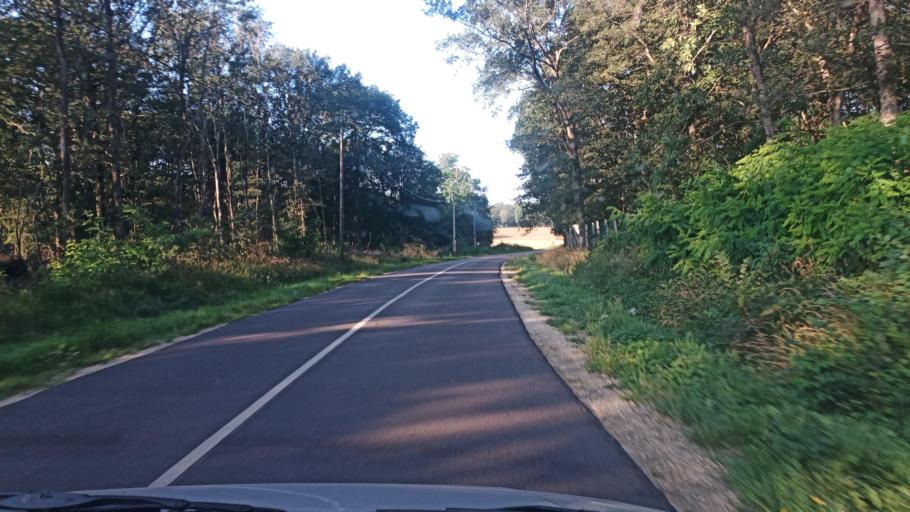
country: FR
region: Bourgogne
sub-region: Departement de l'Yonne
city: Pont-sur-Yonne
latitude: 48.2554
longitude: 3.1698
